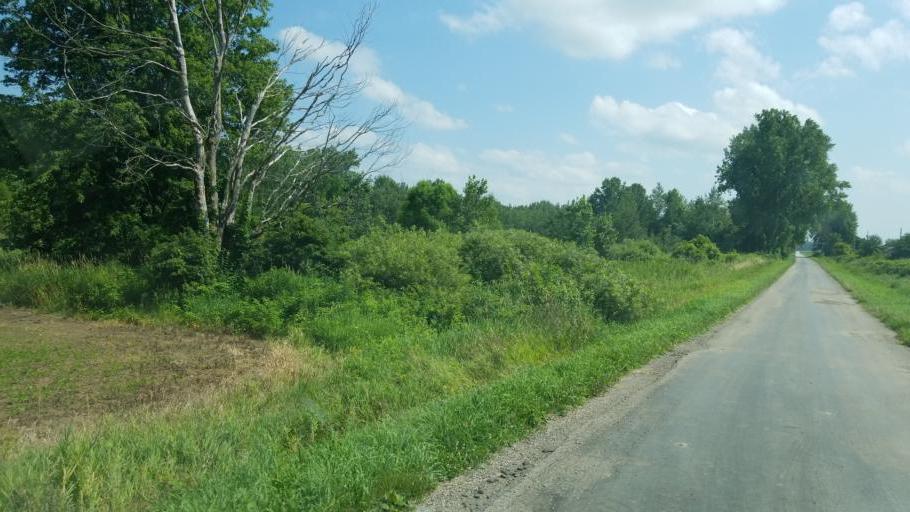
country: US
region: Ohio
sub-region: Huron County
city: Willard
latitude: 41.0101
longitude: -82.7808
